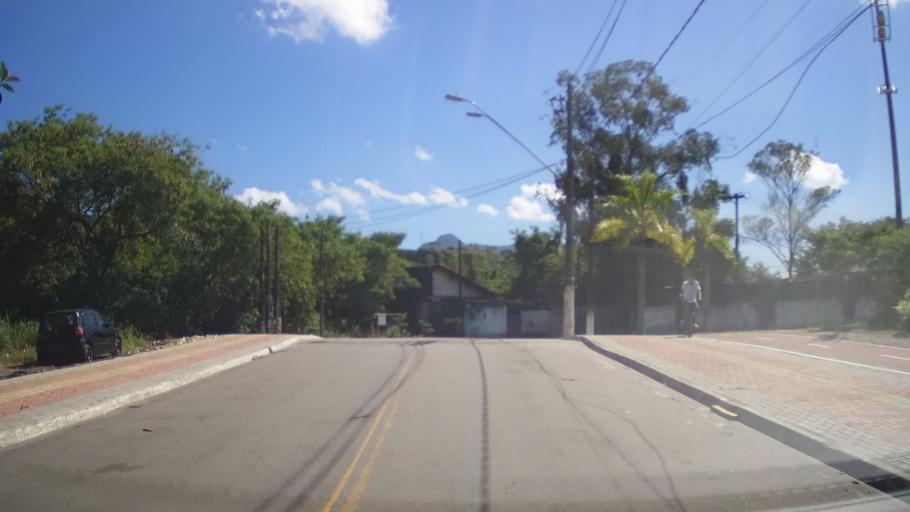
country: BR
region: Sao Paulo
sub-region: Mongagua
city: Mongagua
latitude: -24.0281
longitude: -46.5352
